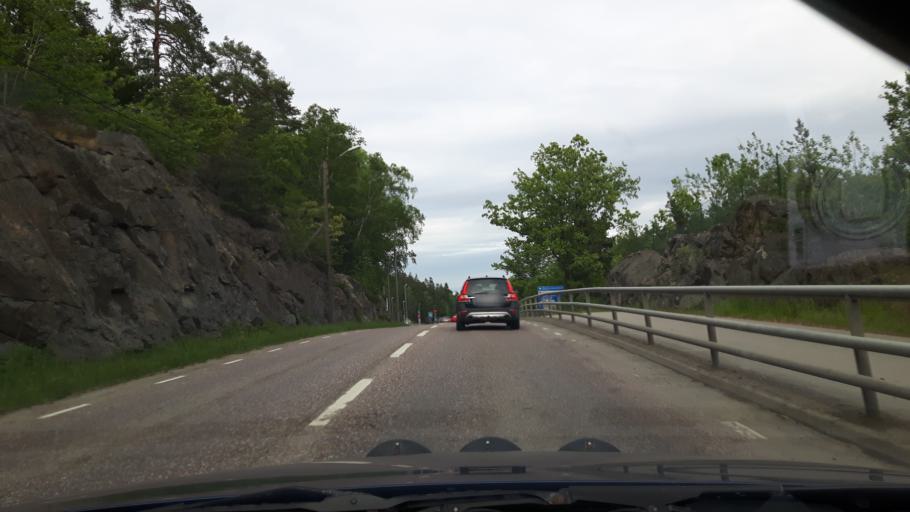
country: SE
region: Stockholm
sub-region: Botkyrka Kommun
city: Tullinge
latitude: 59.2083
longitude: 17.9137
